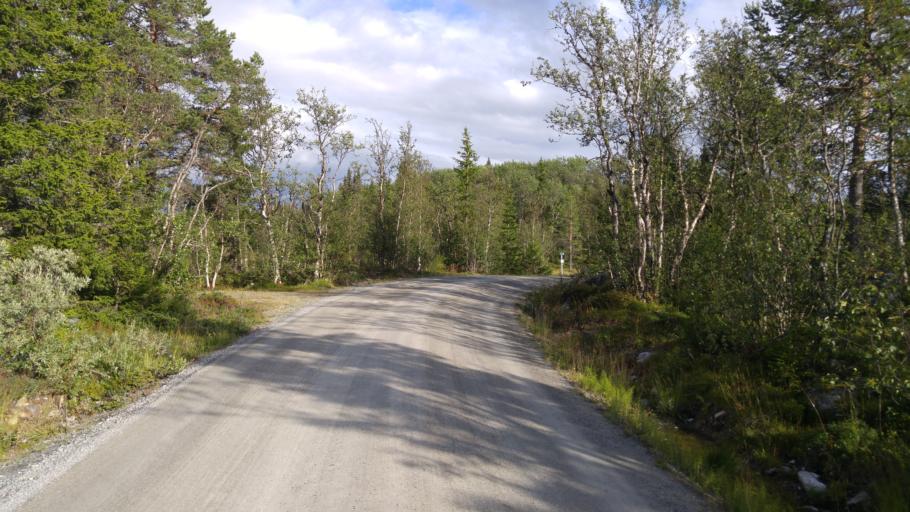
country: NO
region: Buskerud
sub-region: Hemsedal
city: Troim
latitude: 60.8470
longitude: 8.7232
